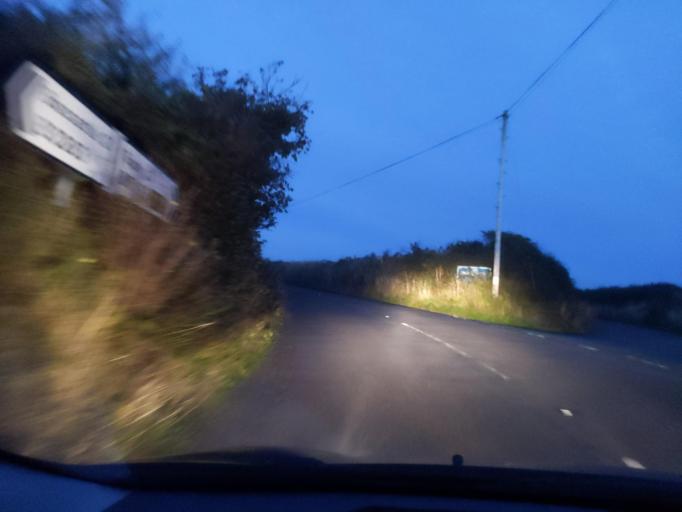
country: GB
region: England
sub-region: Cornwall
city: Camelford
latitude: 50.7006
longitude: -4.6497
